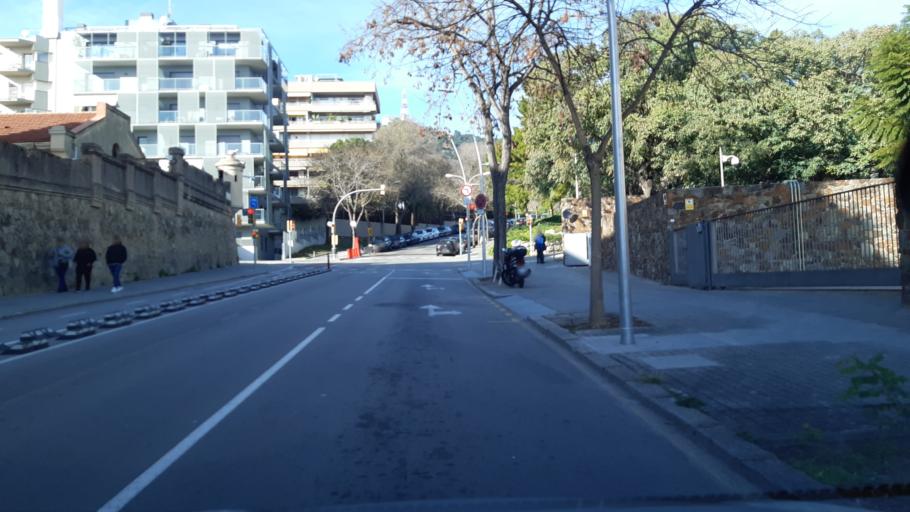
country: ES
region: Catalonia
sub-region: Provincia de Barcelona
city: les Corts
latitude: 41.3877
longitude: 2.1101
